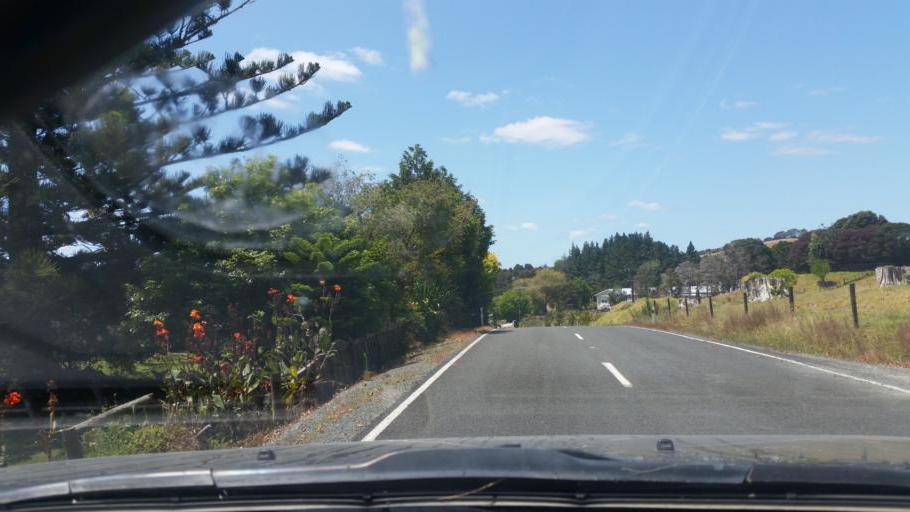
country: NZ
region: Auckland
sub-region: Auckland
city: Wellsford
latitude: -36.1245
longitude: 174.3299
